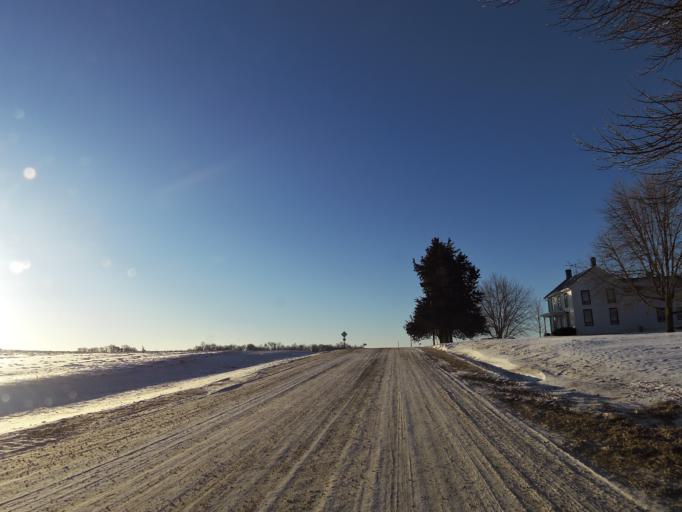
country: US
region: Minnesota
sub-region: Scott County
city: Jordan
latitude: 44.6719
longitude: -93.5418
